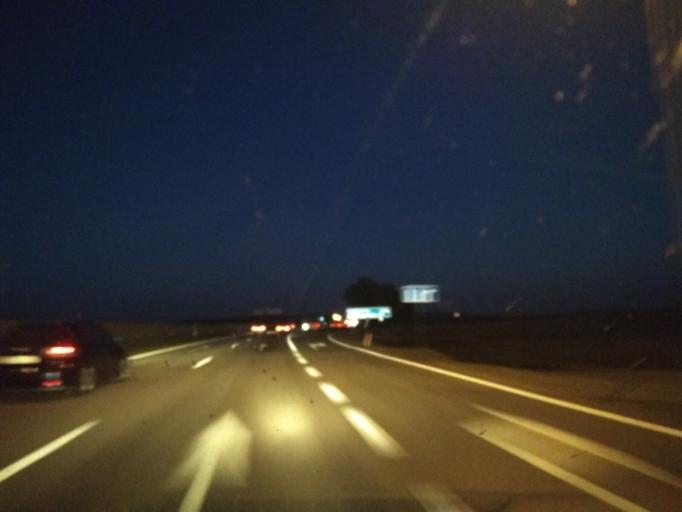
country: BY
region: Minsk
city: Stan'kava
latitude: 53.7067
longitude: 27.2184
